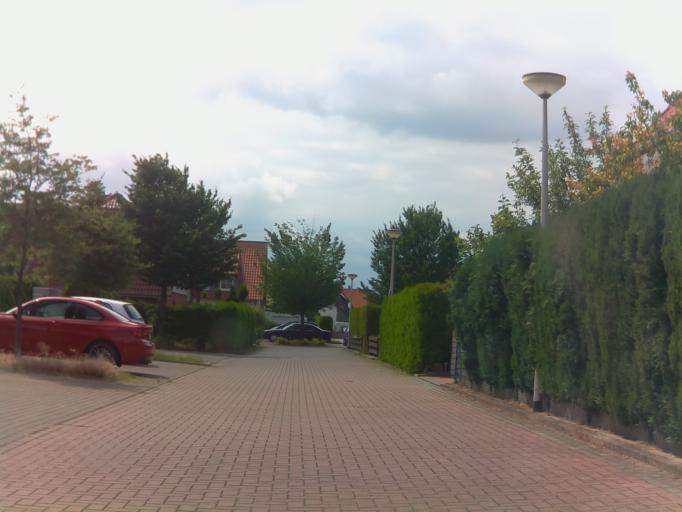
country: DE
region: Lower Saxony
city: Harsum
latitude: 52.1733
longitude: 9.9966
